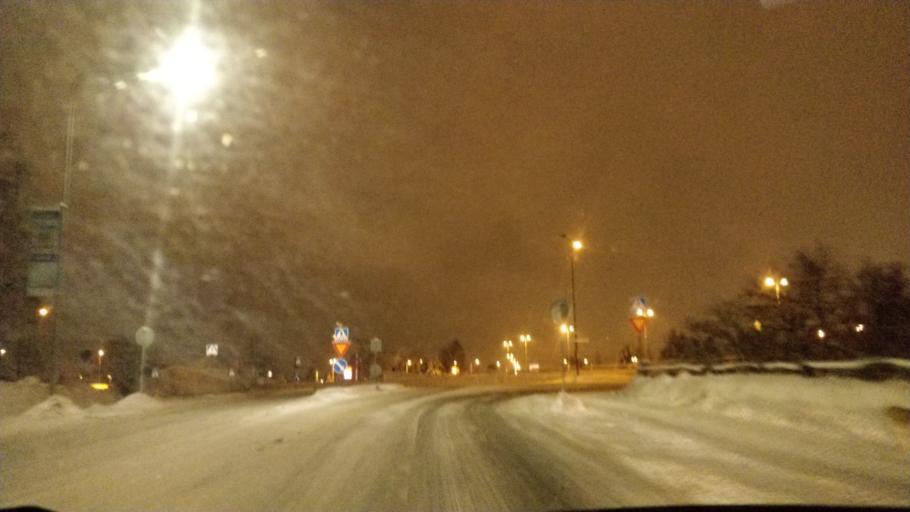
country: FI
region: Lapland
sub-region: Rovaniemi
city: Rovaniemi
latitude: 66.4993
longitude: 25.7184
